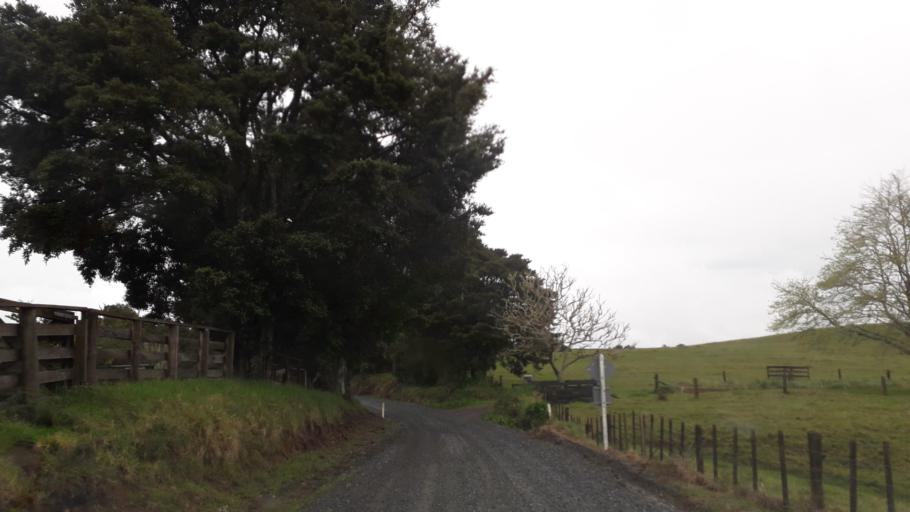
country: NZ
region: Northland
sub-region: Far North District
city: Waimate North
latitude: -35.1365
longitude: 173.7130
